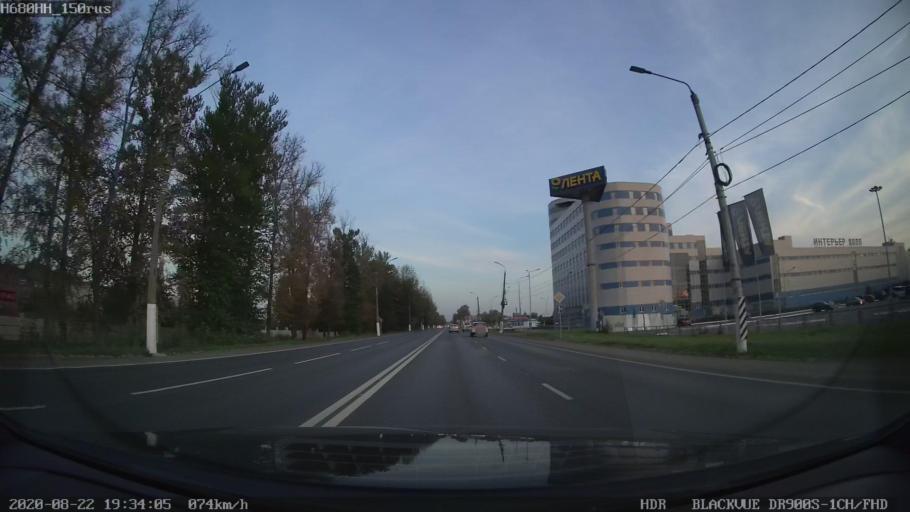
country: RU
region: Tverskaya
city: Tver
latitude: 56.8441
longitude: 35.9502
